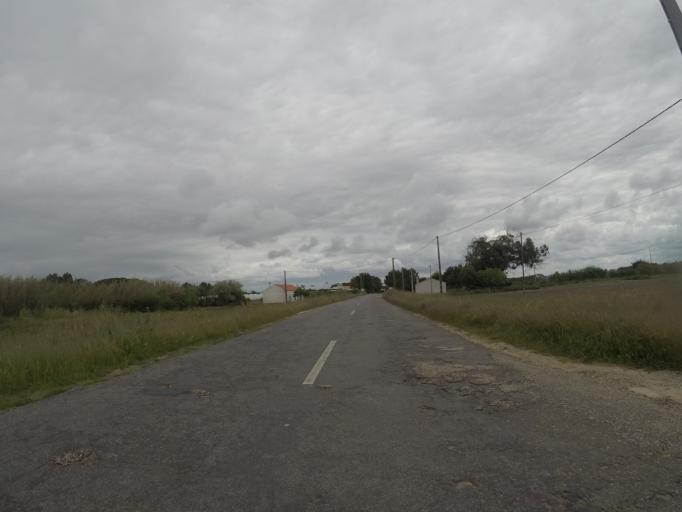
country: PT
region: Beja
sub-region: Odemira
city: Vila Nova de Milfontes
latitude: 37.6138
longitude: -8.7907
